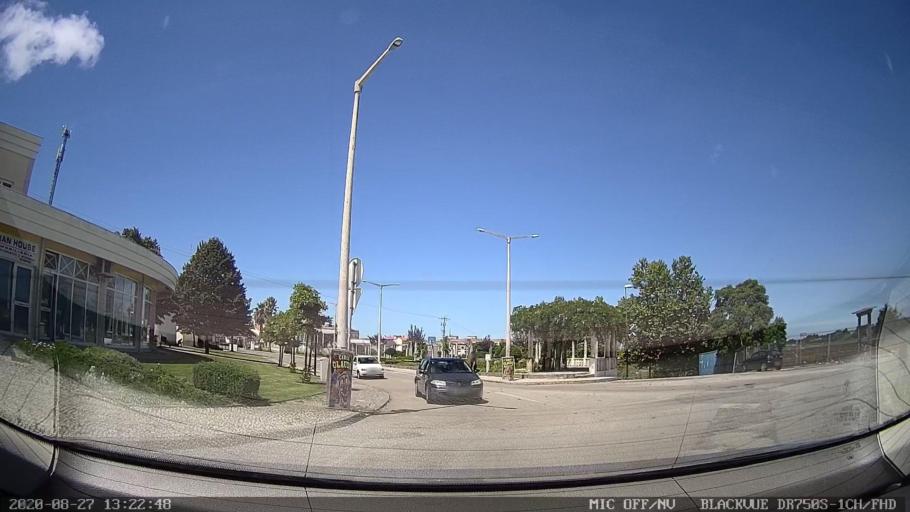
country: PT
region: Aveiro
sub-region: Vagos
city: Vagos
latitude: 40.5530
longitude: -8.6782
